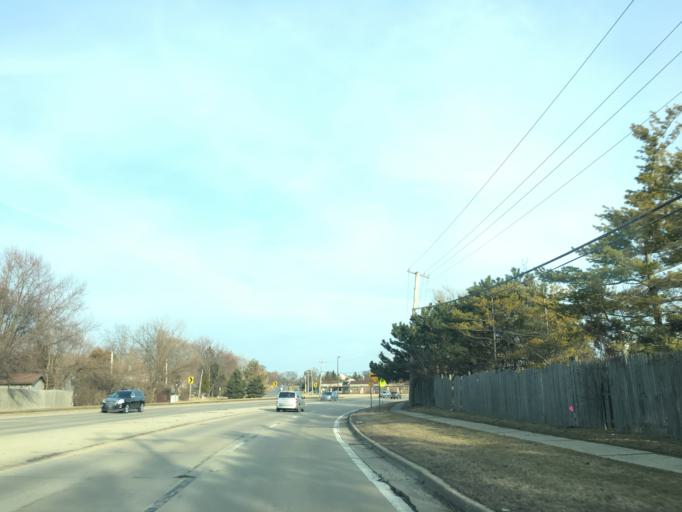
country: US
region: Illinois
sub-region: Cook County
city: Streamwood
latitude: 42.0318
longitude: -88.1586
